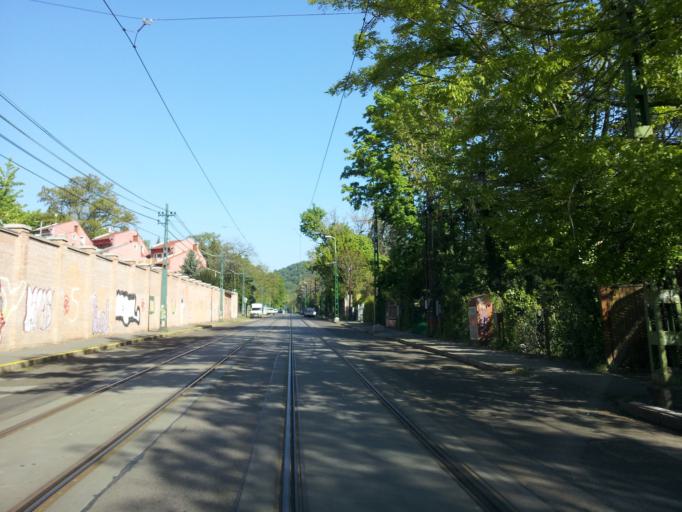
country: HU
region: Budapest
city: Budapest XII. keruelet
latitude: 47.5332
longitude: 18.9797
